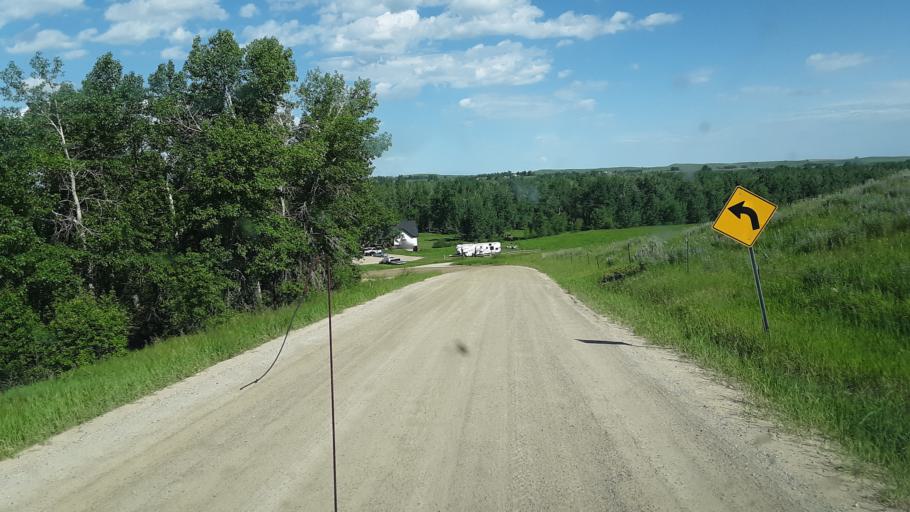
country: US
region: Montana
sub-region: Carbon County
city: Red Lodge
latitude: 45.2792
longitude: -109.2039
